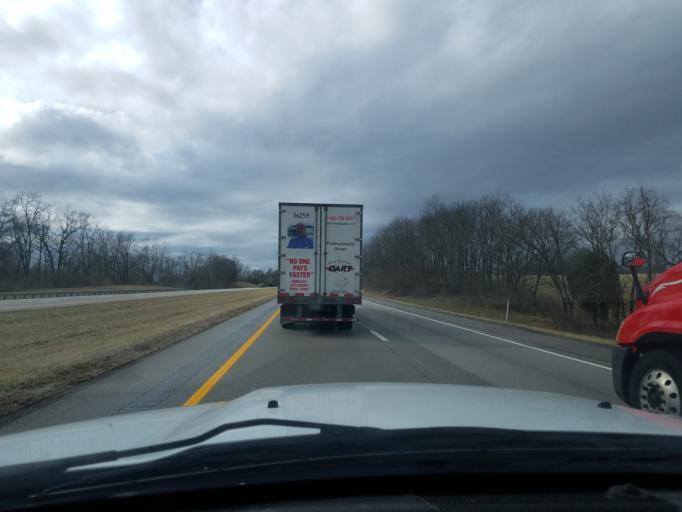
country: US
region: Kentucky
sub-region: Montgomery County
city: Mount Sterling
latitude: 38.0914
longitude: -83.8802
